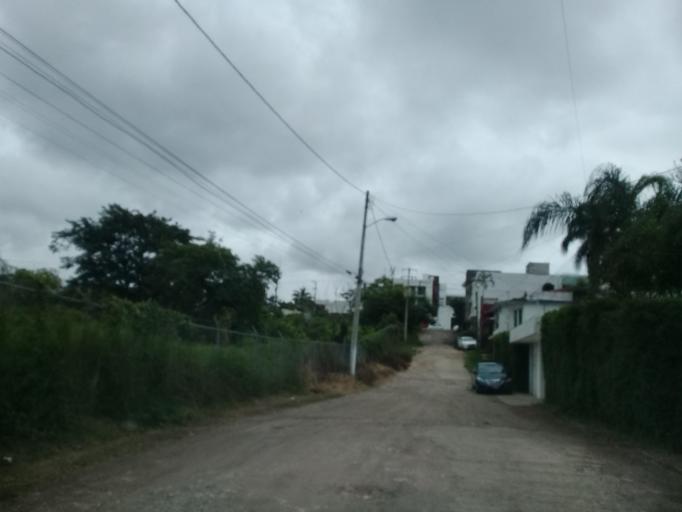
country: MX
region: Veracruz
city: El Castillo
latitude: 19.5281
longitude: -96.8786
